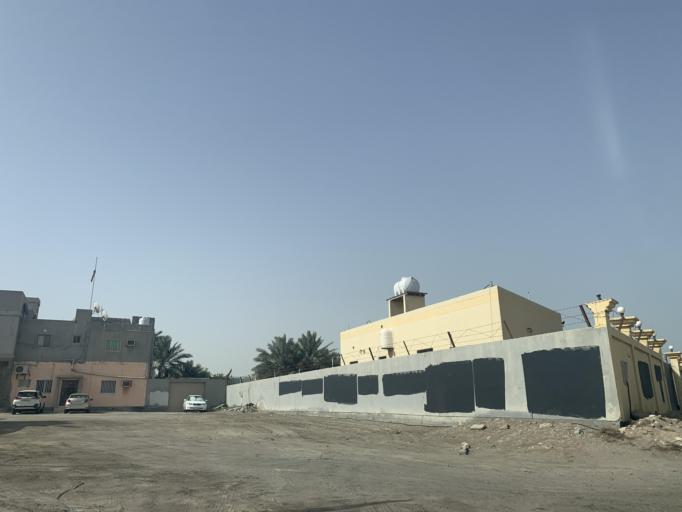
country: BH
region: Northern
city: Sitrah
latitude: 26.1621
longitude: 50.6069
